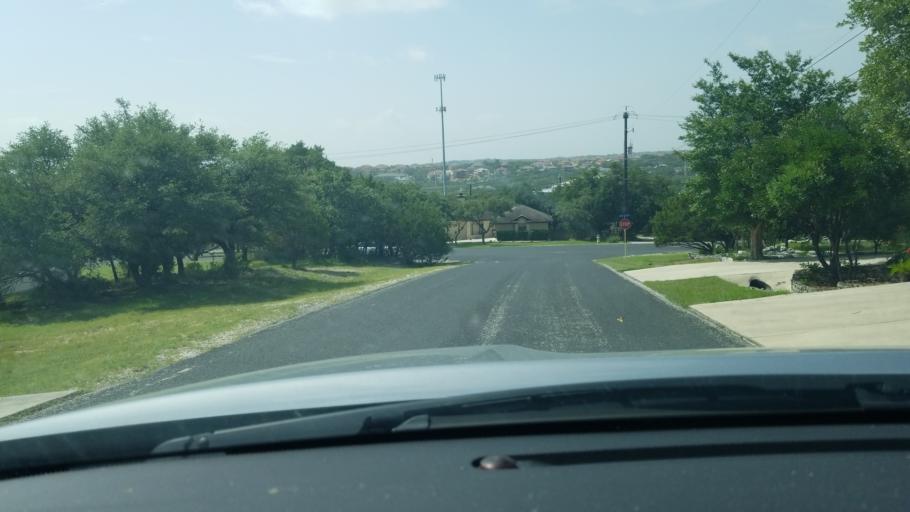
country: US
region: Texas
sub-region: Bexar County
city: Timberwood Park
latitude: 29.6853
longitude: -98.4917
